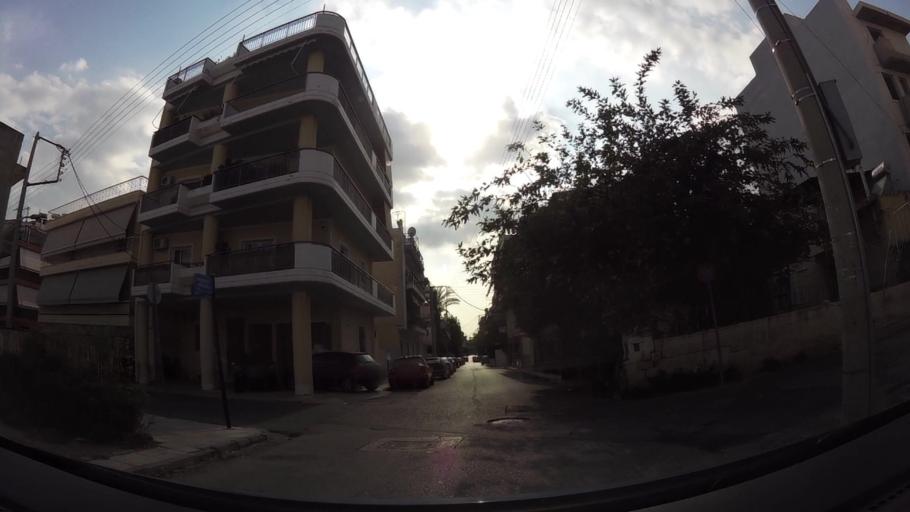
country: GR
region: Attica
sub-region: Nomarchia Athinas
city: Ilion
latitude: 38.0368
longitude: 23.6973
